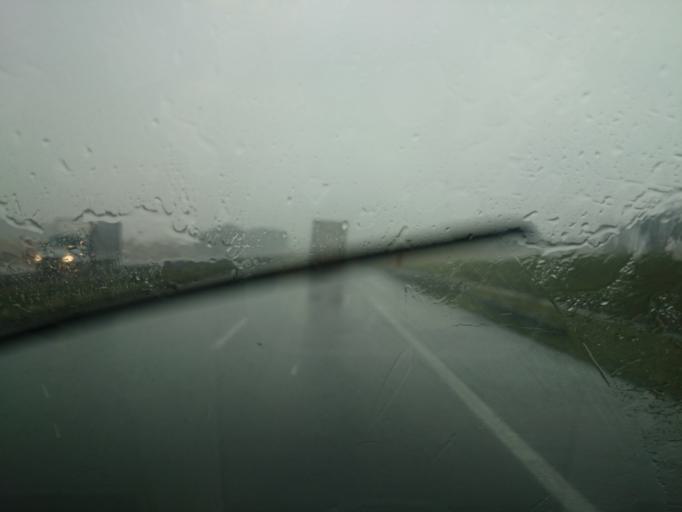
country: PL
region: Opole Voivodeship
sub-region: Powiat strzelecki
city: Strzelce Opolskie
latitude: 50.4587
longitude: 18.2570
